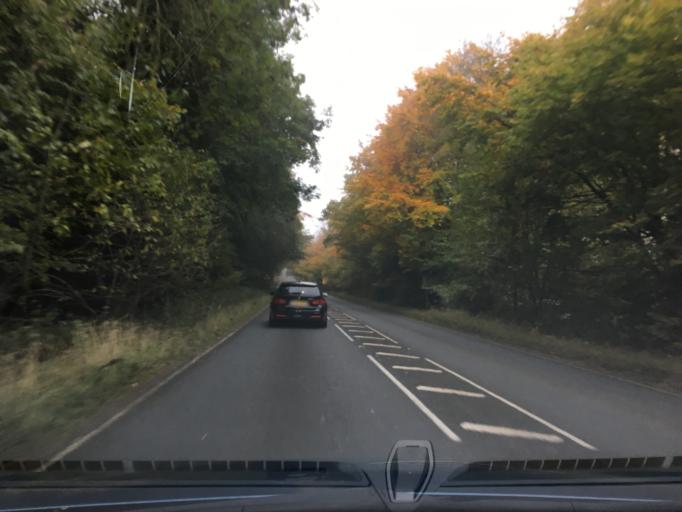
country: GB
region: England
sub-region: Hampshire
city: Four Marks
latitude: 51.1173
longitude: -1.0285
